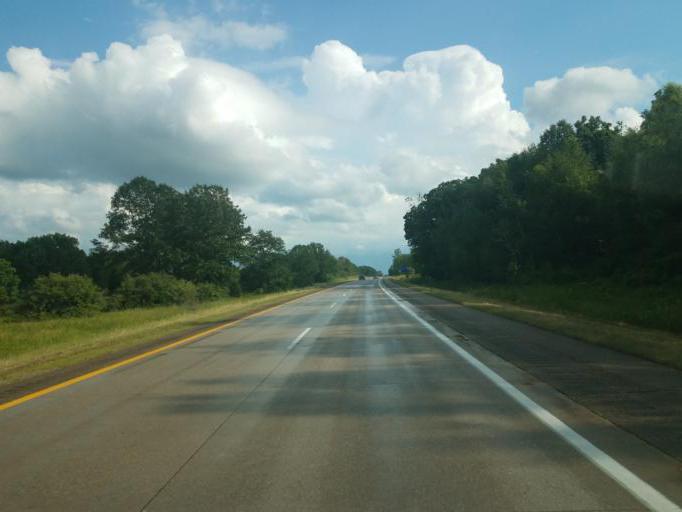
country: US
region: Michigan
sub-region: Calhoun County
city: Marshall
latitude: 42.2189
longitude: -84.9823
